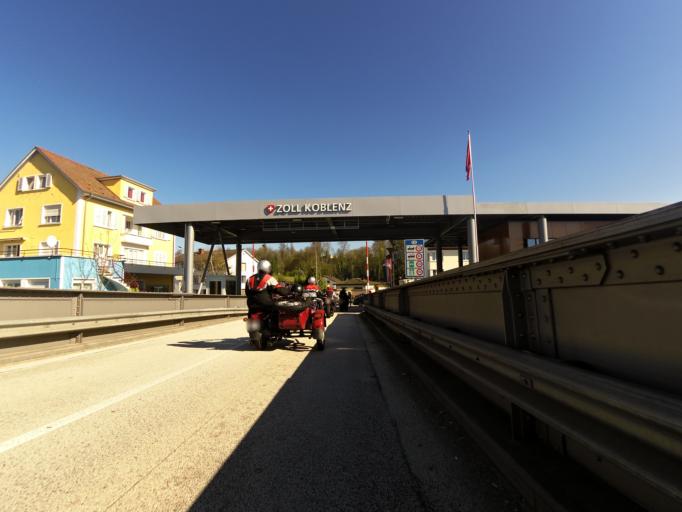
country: CH
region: Aargau
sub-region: Bezirk Zurzach
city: Koblenz
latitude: 47.6083
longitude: 8.2337
